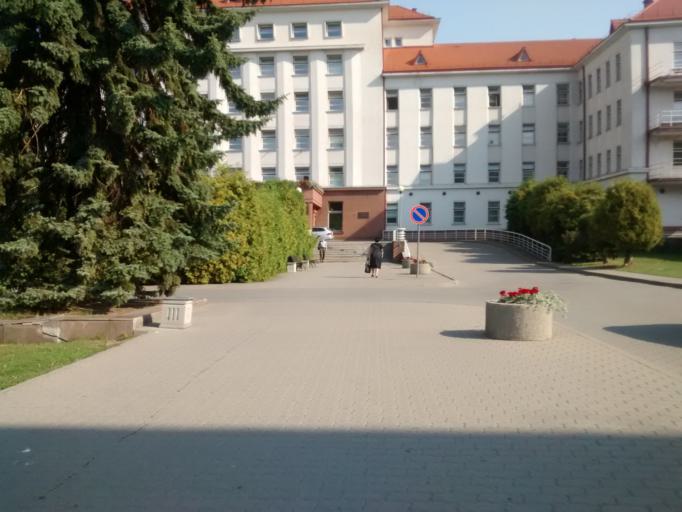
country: LT
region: Kauno apskritis
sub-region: Kaunas
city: Eiguliai
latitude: 54.9179
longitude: 23.9212
